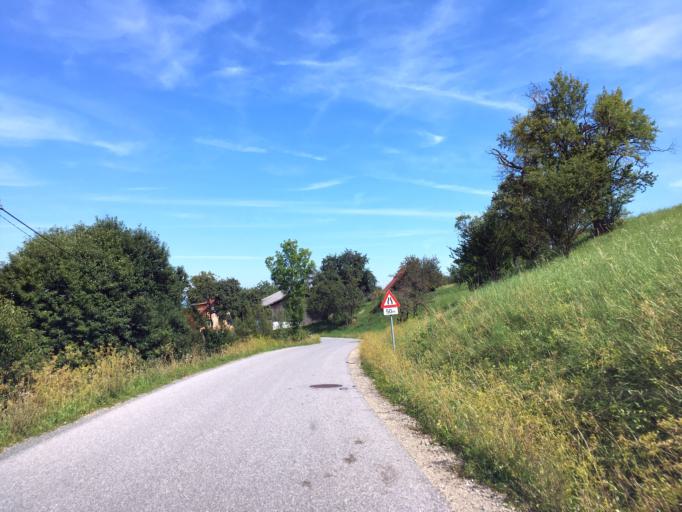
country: AT
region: Styria
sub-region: Politischer Bezirk Leibnitz
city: Sankt Nikolai im Sausal
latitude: 46.8042
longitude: 15.4369
